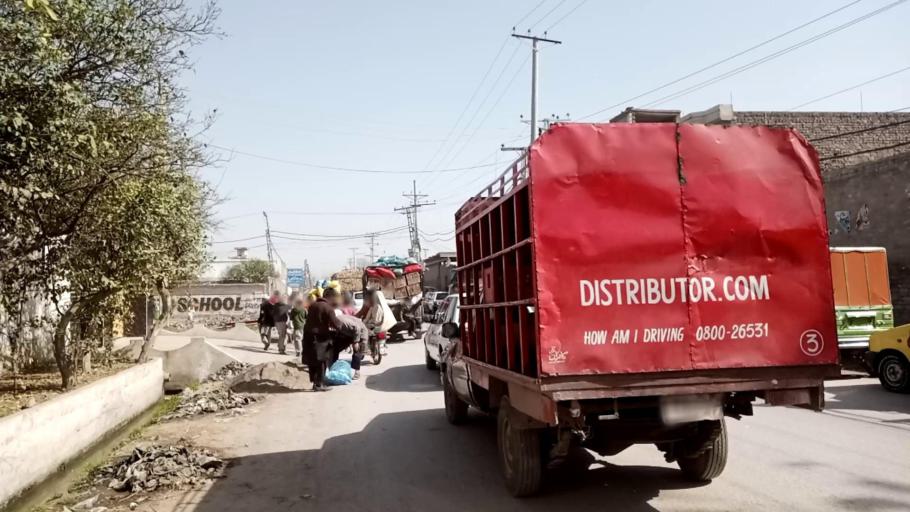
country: PK
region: Khyber Pakhtunkhwa
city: Peshawar
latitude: 34.0098
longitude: 71.6459
